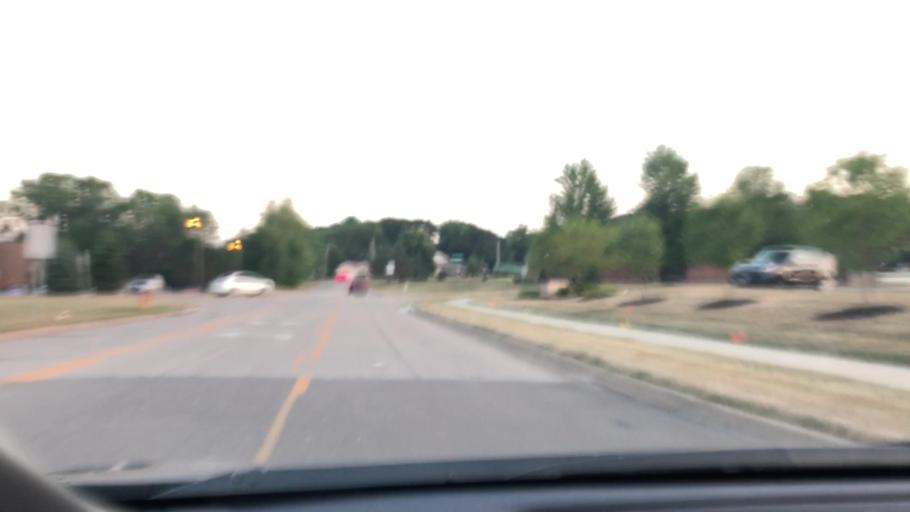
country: US
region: Ohio
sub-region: Summit County
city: Green
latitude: 40.9616
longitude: -81.4678
